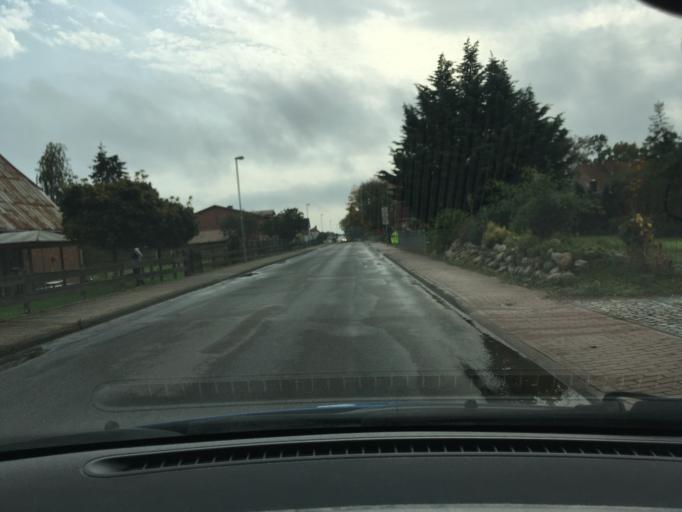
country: DE
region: Schleswig-Holstein
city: Tensfeld
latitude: 54.0452
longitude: 10.3177
